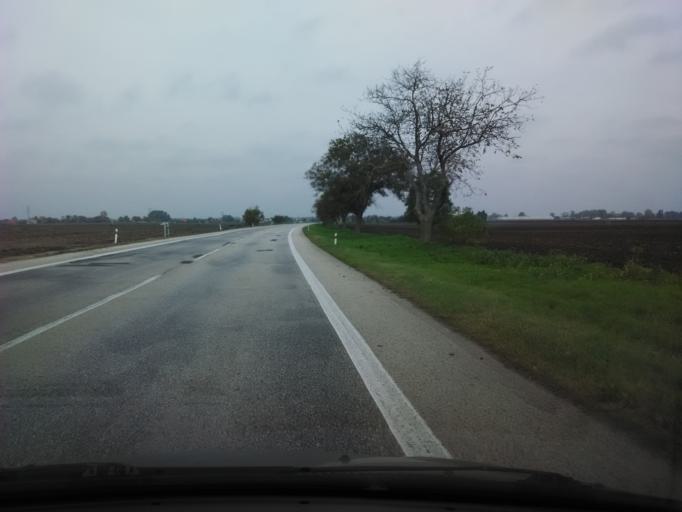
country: SK
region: Nitriansky
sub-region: Okres Komarno
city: Hurbanovo
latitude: 47.8321
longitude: 18.1721
